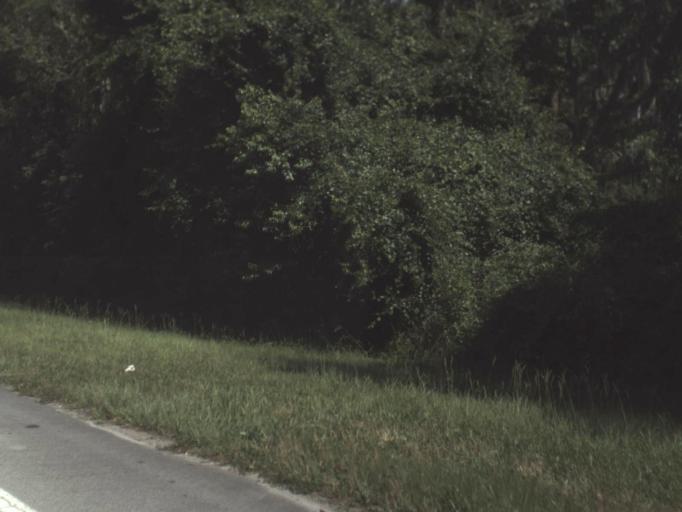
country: US
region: Florida
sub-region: Alachua County
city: Waldo
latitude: 29.7136
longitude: -82.1189
